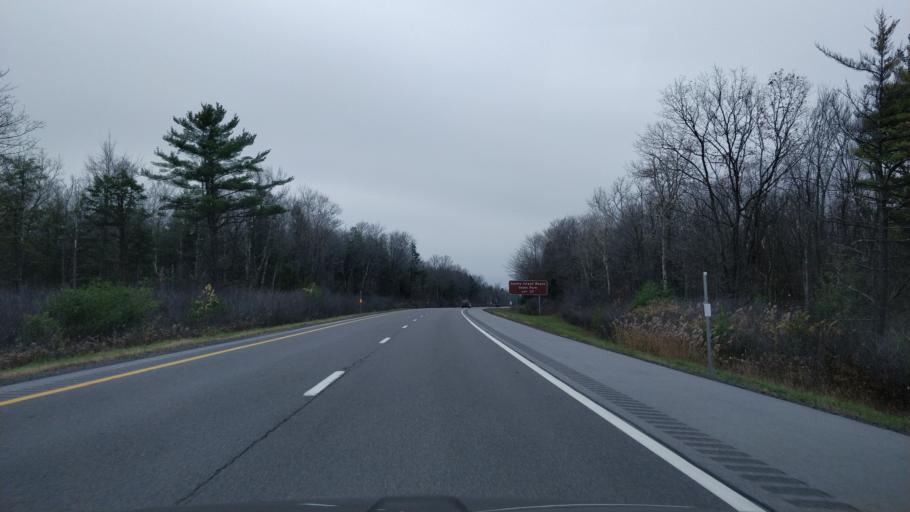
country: US
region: New York
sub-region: Oswego County
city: Pulaski
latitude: 43.6691
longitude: -76.0708
